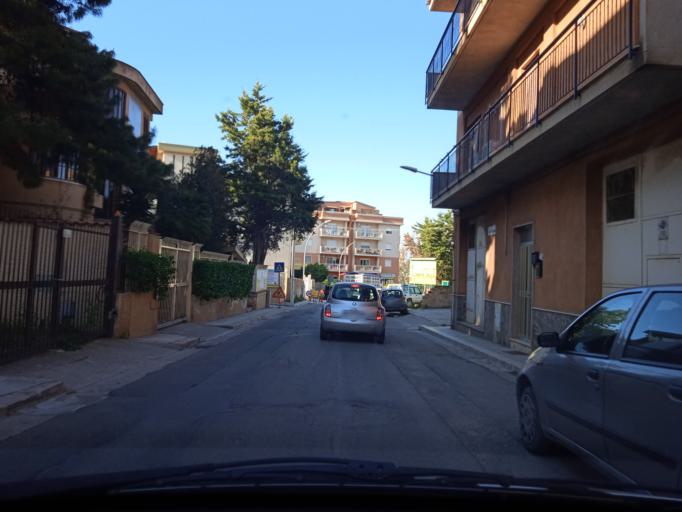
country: IT
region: Sicily
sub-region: Palermo
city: Villabate
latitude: 38.0816
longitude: 13.4488
